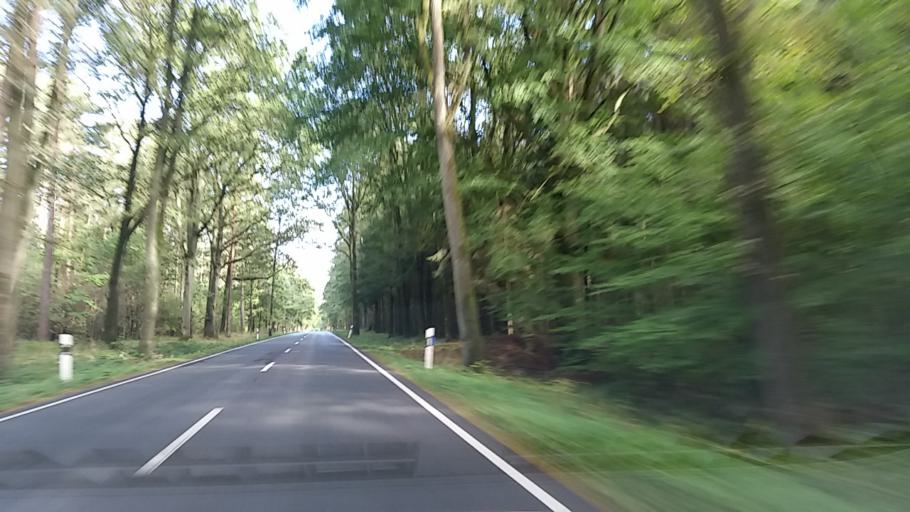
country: DE
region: Lower Saxony
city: Neuenkirchen
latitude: 53.0240
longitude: 9.6773
